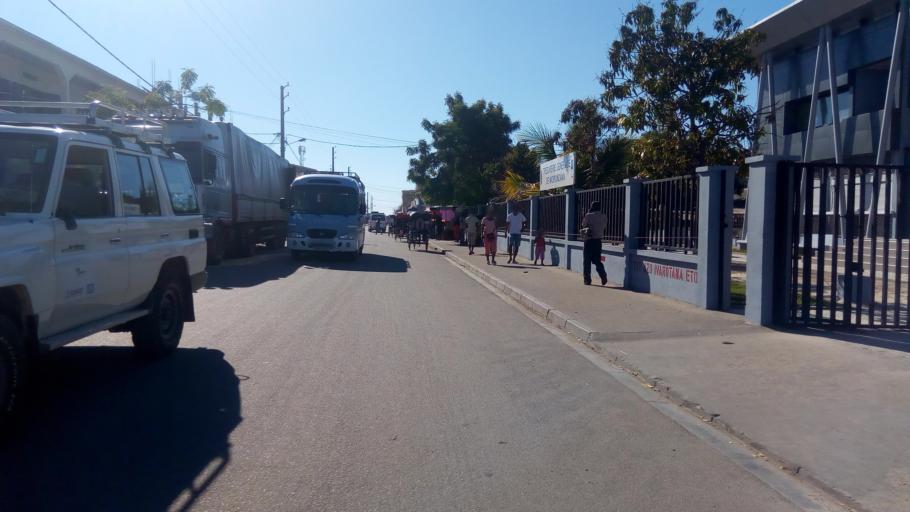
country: MG
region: Menabe
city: Morondava
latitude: -20.2924
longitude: 44.2768
